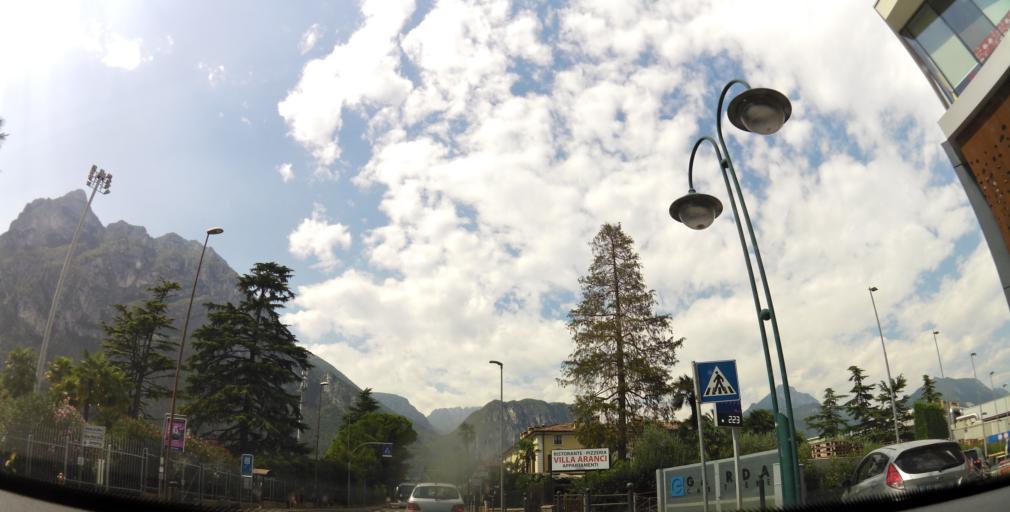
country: IT
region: Trentino-Alto Adige
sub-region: Provincia di Trento
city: Riva del Garda
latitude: 45.8829
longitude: 10.8533
